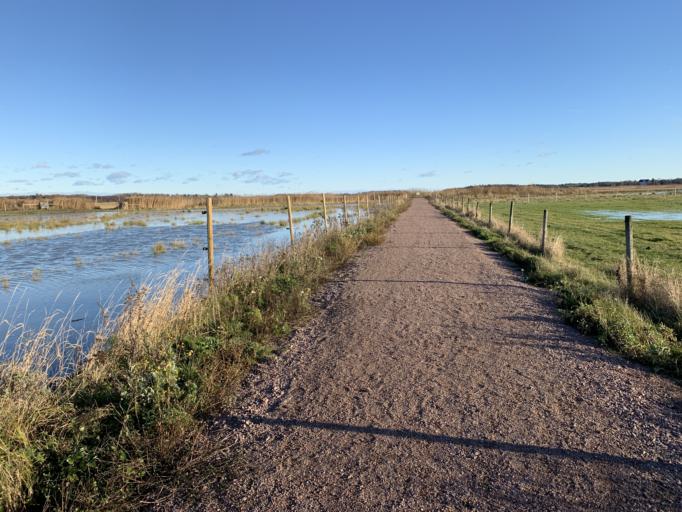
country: SE
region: Soedermanland
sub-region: Eskilstuna Kommun
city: Torshalla
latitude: 59.5232
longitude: 16.4487
